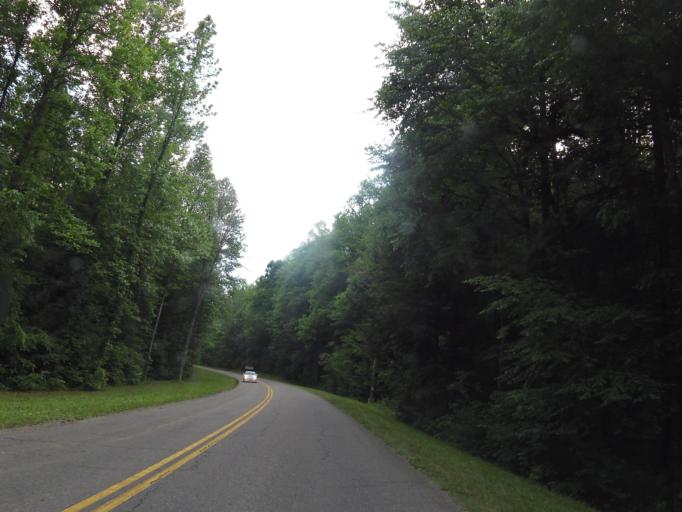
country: US
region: Tennessee
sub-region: Sevier County
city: Gatlinburg
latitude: 35.6863
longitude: -83.5415
